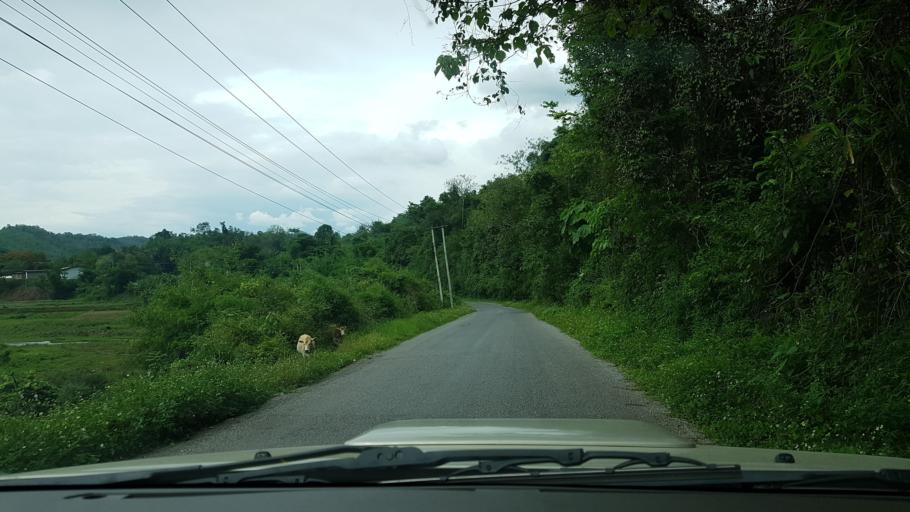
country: LA
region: Loungnamtha
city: Muang Nale
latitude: 20.3783
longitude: 101.7391
